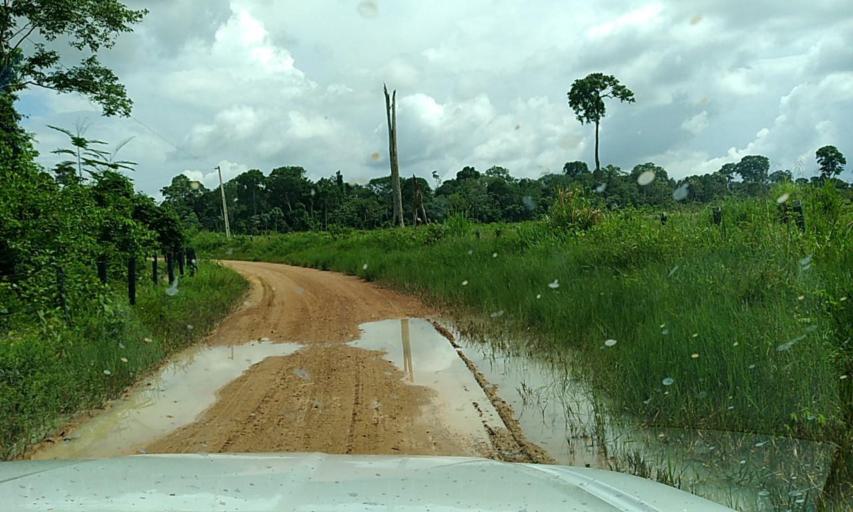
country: BR
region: Para
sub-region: Senador Jose Porfirio
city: Senador Jose Porfirio
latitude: -2.5194
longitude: -51.8380
